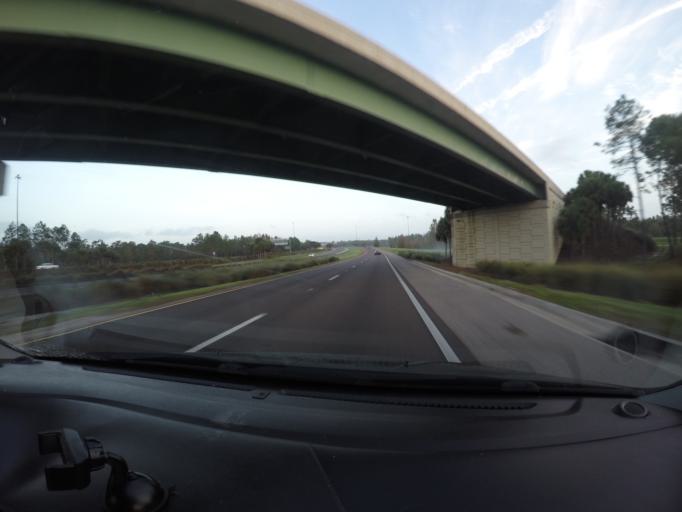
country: US
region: Florida
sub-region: Orange County
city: Conway
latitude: 28.4530
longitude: -81.2303
